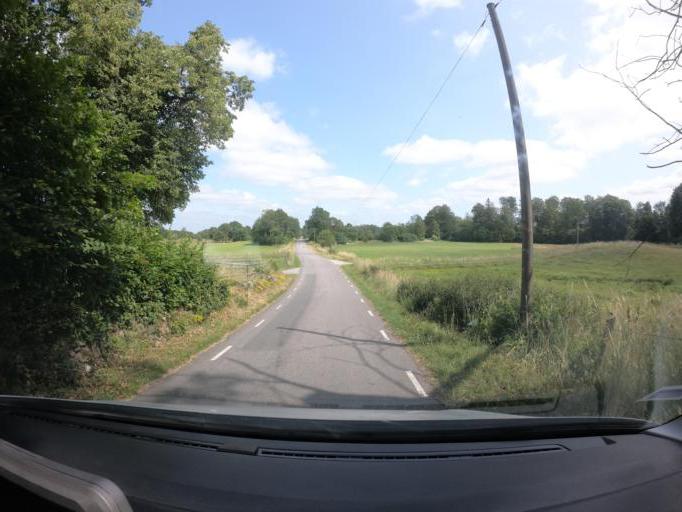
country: SE
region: Skane
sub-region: Hassleholms Kommun
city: Sosdala
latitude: 56.0315
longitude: 13.6293
